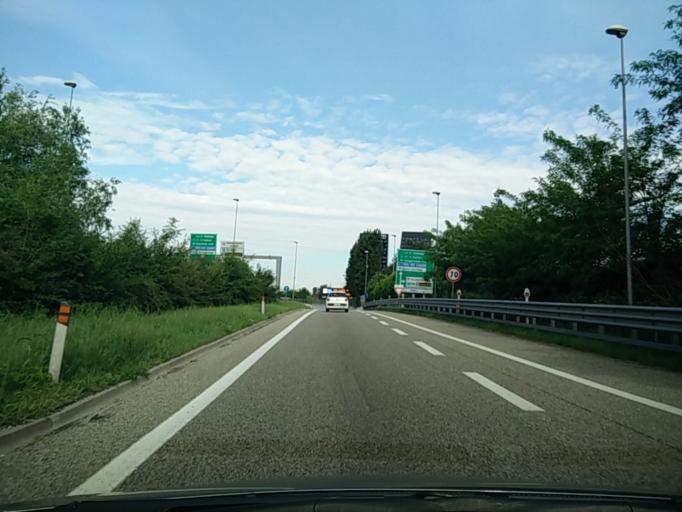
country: IT
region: Lombardy
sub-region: Citta metropolitana di Milano
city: Pero
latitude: 45.5155
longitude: 9.0825
